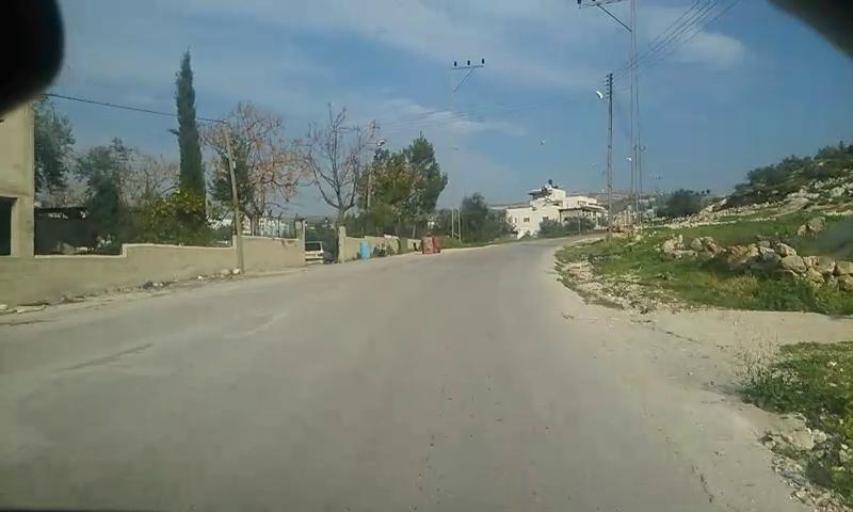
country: PS
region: West Bank
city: Nuba
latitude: 31.6143
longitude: 35.0308
